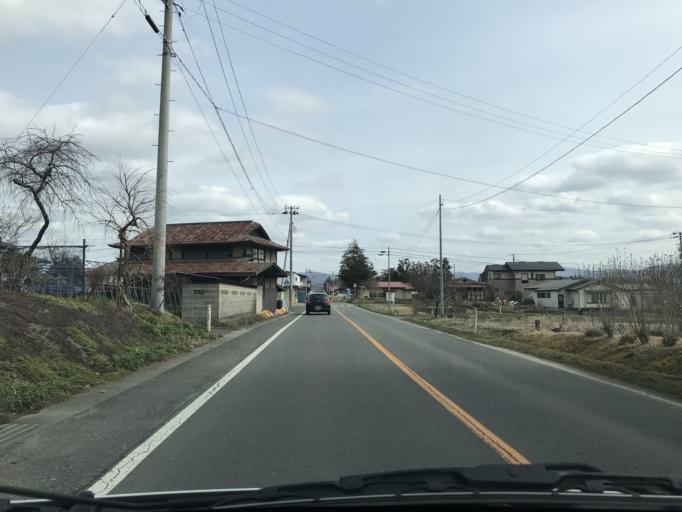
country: JP
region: Iwate
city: Mizusawa
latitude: 39.2162
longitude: 141.2140
